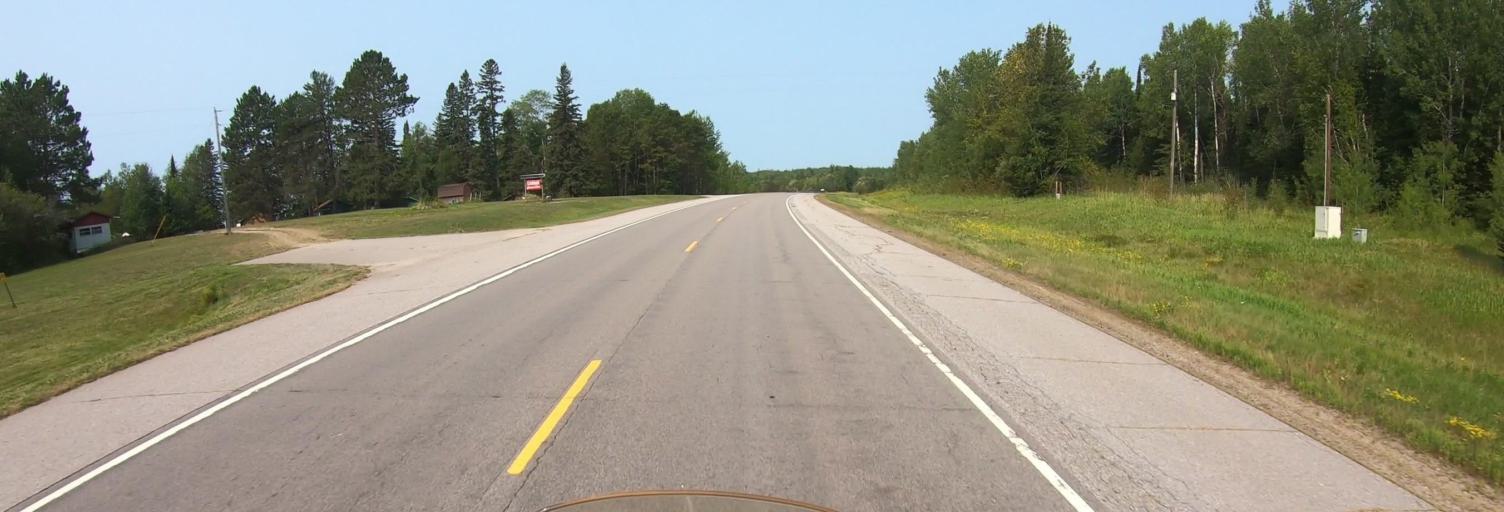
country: CA
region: Ontario
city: Fort Frances
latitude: 48.2185
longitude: -92.9147
